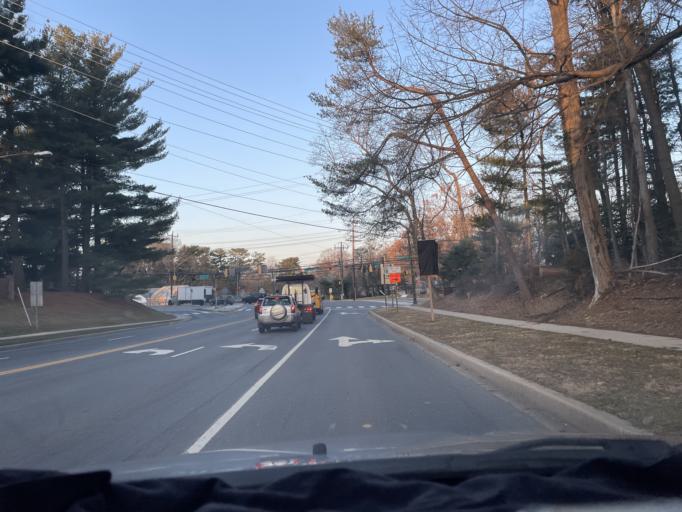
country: US
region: Maryland
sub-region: Montgomery County
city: North Bethesda
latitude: 39.0449
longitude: -77.1196
